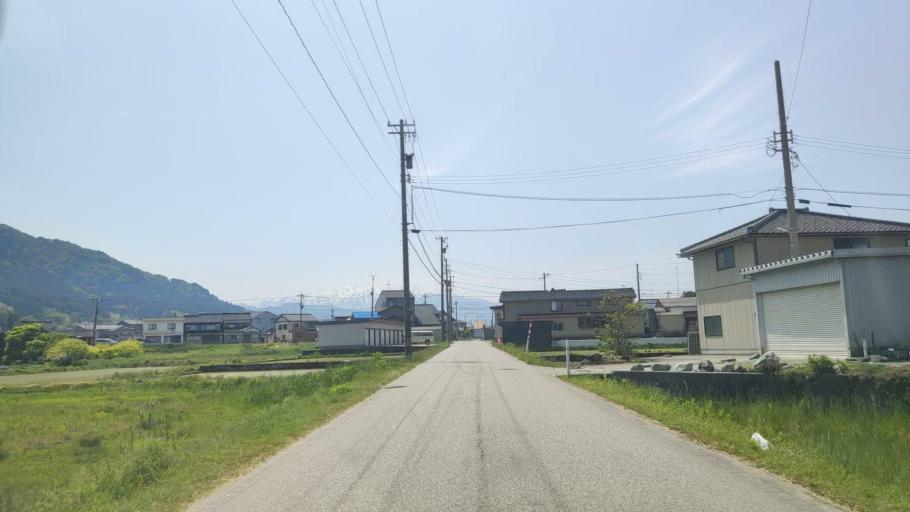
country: JP
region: Toyama
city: Nyuzen
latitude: 36.9590
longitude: 137.5681
